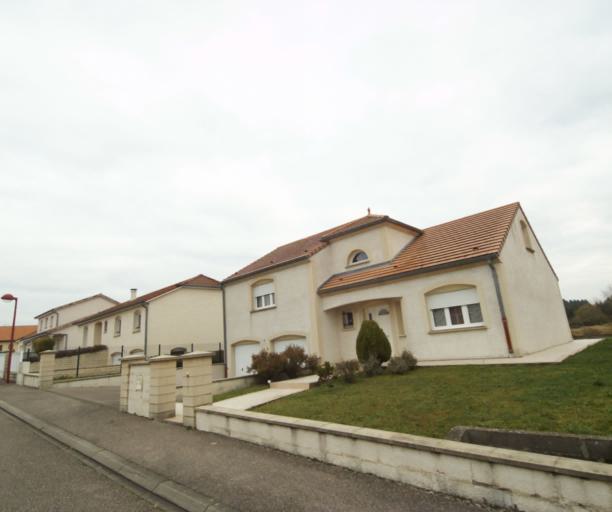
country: FR
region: Lorraine
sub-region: Departement de Meurthe-et-Moselle
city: Mancieulles
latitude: 49.2785
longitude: 5.9022
